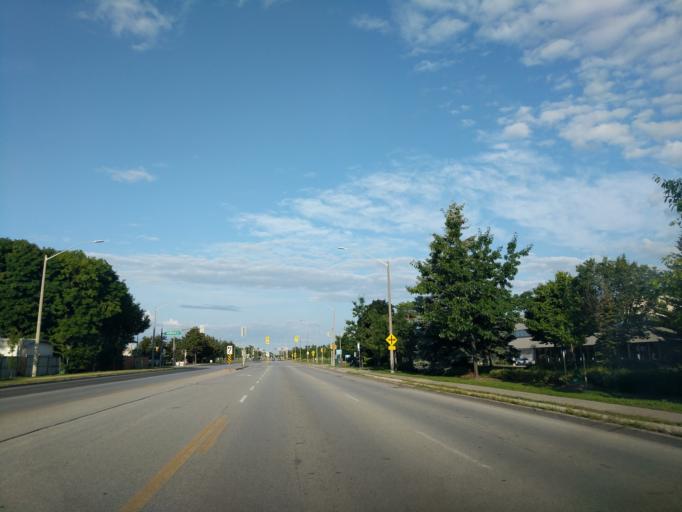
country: CA
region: Ontario
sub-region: York
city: Richmond Hill
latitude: 43.8922
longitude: -79.4301
